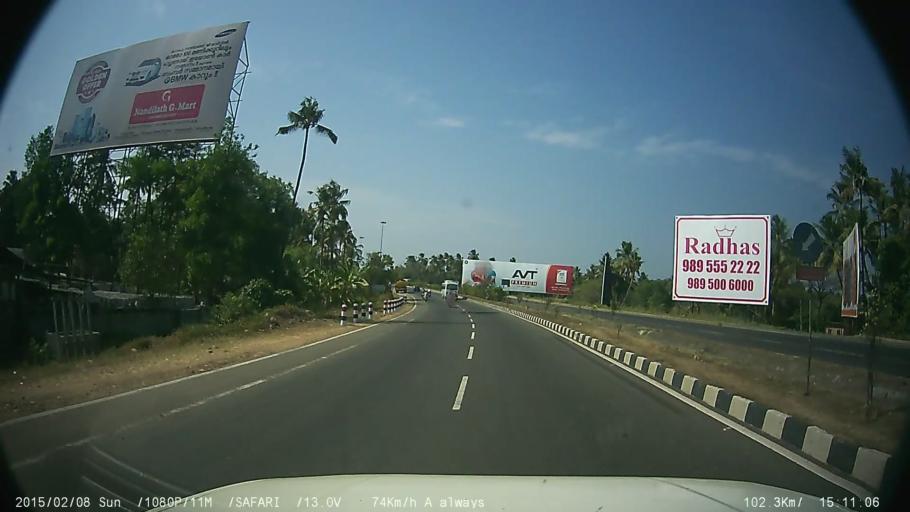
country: IN
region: Kerala
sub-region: Thrissur District
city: Irinjalakuda
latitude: 10.4091
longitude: 76.2740
